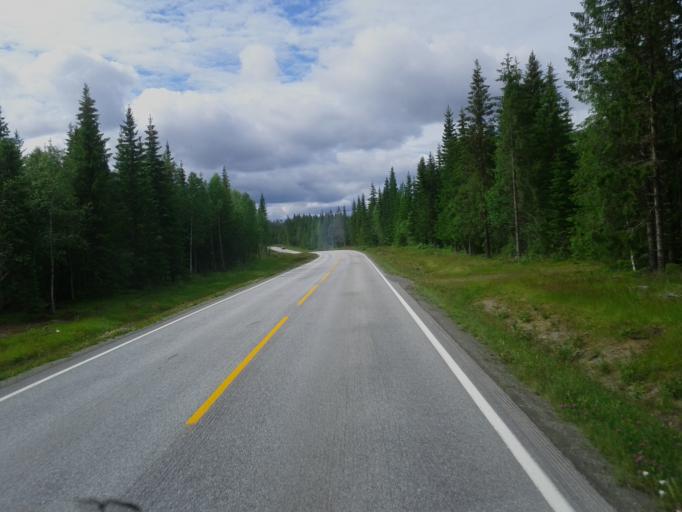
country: NO
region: Nord-Trondelag
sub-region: Hoylandet
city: Hoylandet
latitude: 64.6874
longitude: 12.7355
